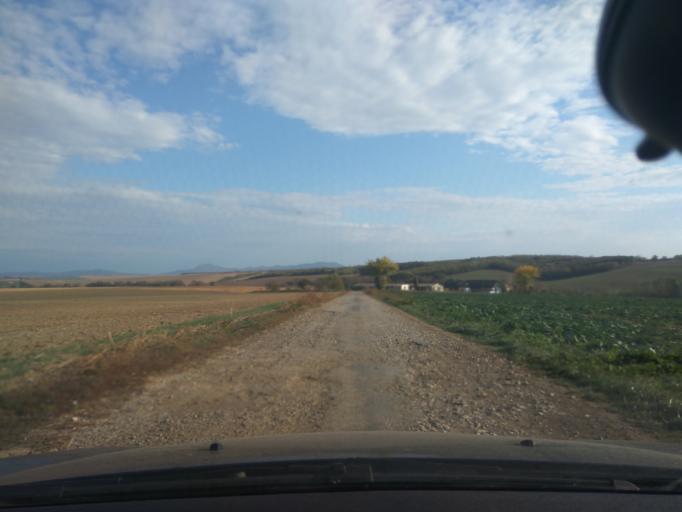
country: SK
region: Trnavsky
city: Hlohovec
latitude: 48.4477
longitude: 17.9231
